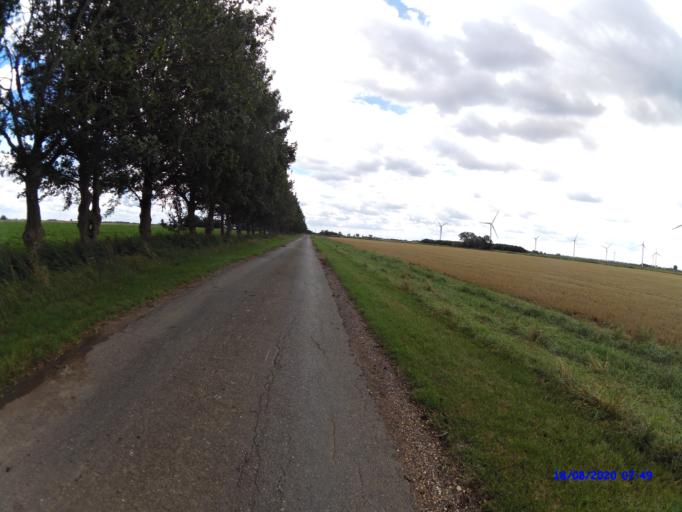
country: GB
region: England
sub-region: Cambridgeshire
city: Whittlesey
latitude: 52.5209
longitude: -0.0956
